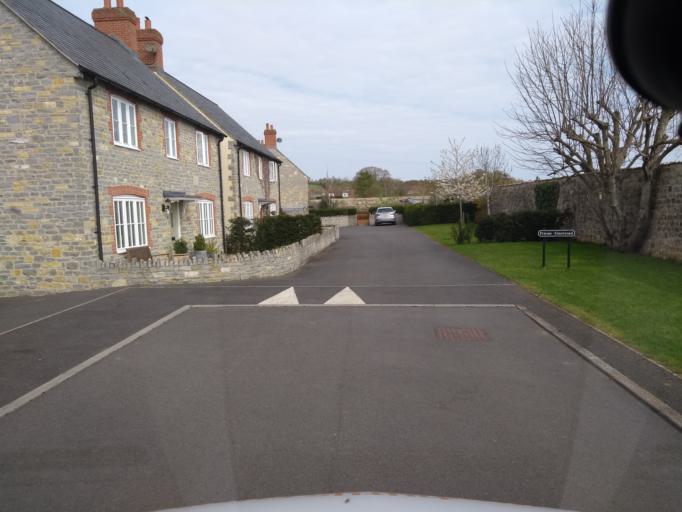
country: GB
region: England
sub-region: Somerset
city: Langport
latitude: 51.0454
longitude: -2.8185
